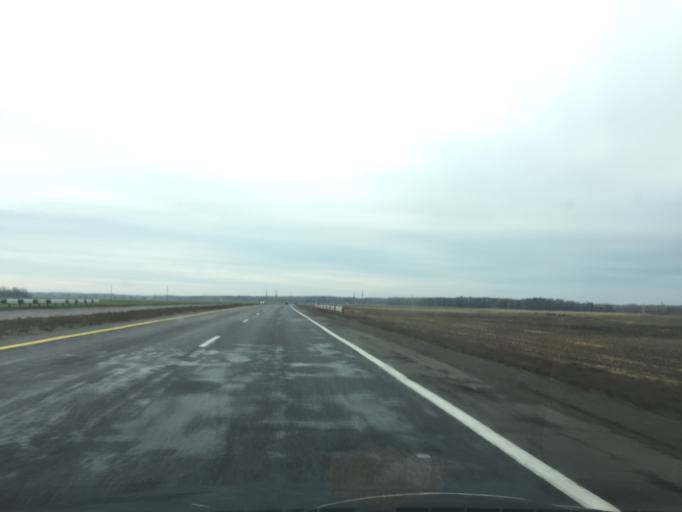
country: BY
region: Gomel
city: Horad Rechytsa
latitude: 52.3404
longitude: 30.5559
